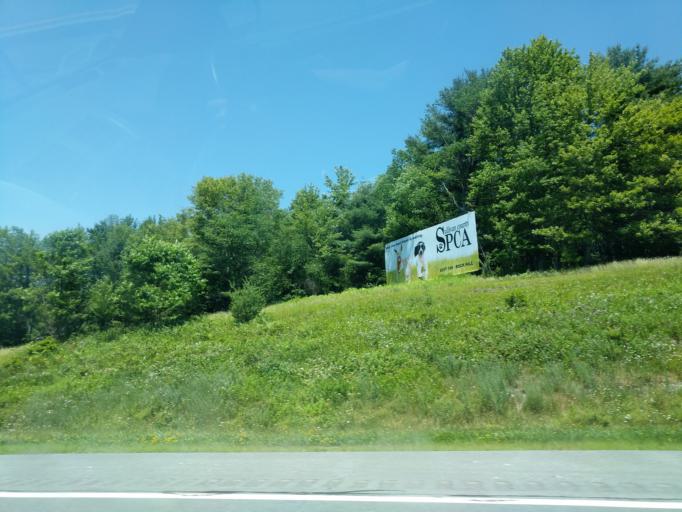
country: US
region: New York
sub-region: Sullivan County
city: Rock Hill
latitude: 41.6278
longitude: -74.6047
